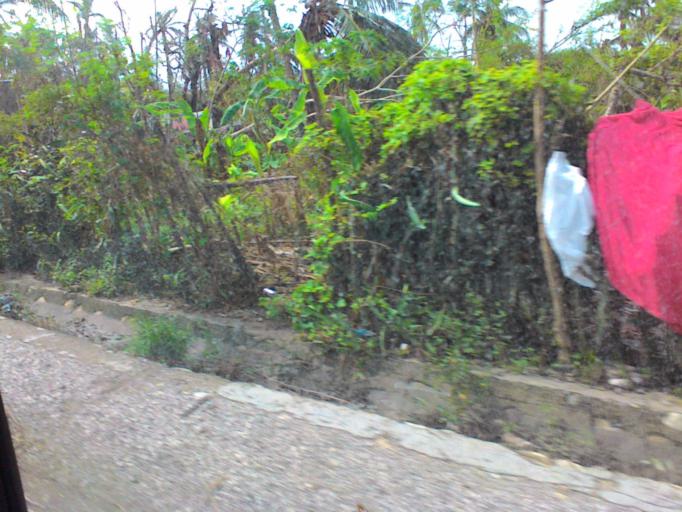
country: HT
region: Sud
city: Les Cayes
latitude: 18.2225
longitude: -73.7691
